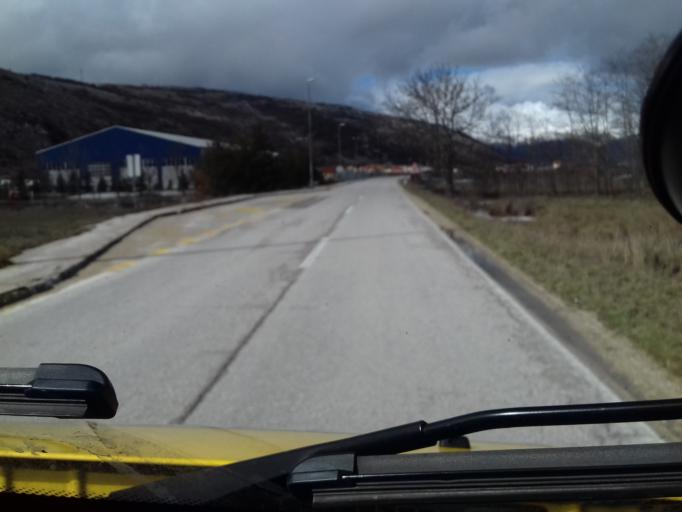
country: BA
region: Federation of Bosnia and Herzegovina
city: Tomislavgrad
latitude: 43.6512
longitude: 17.2227
